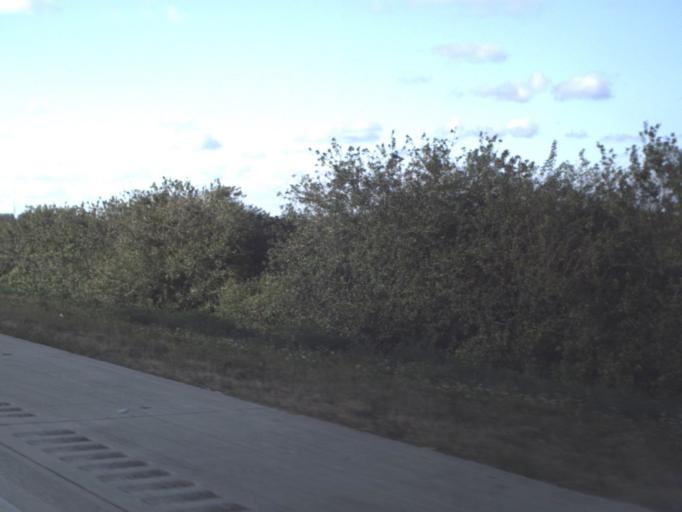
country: US
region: Florida
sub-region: Brevard County
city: Cocoa West
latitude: 28.3181
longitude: -80.7671
